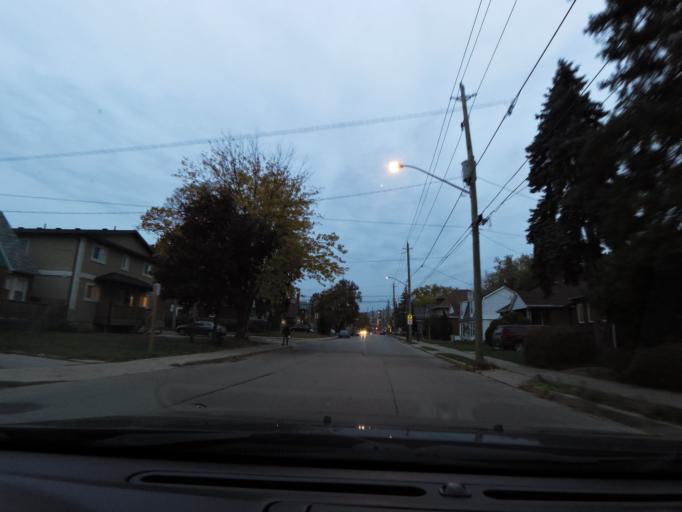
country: CA
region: Ontario
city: Hamilton
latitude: 43.2552
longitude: -79.9207
